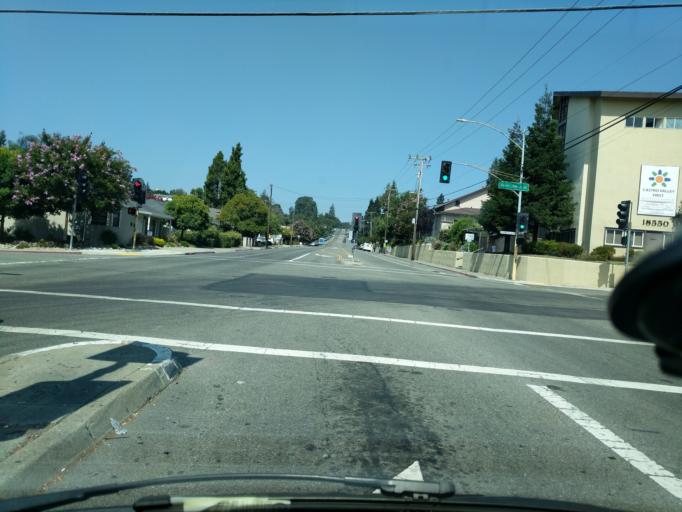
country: US
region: California
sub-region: Alameda County
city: Castro Valley
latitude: 37.7093
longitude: -122.0740
